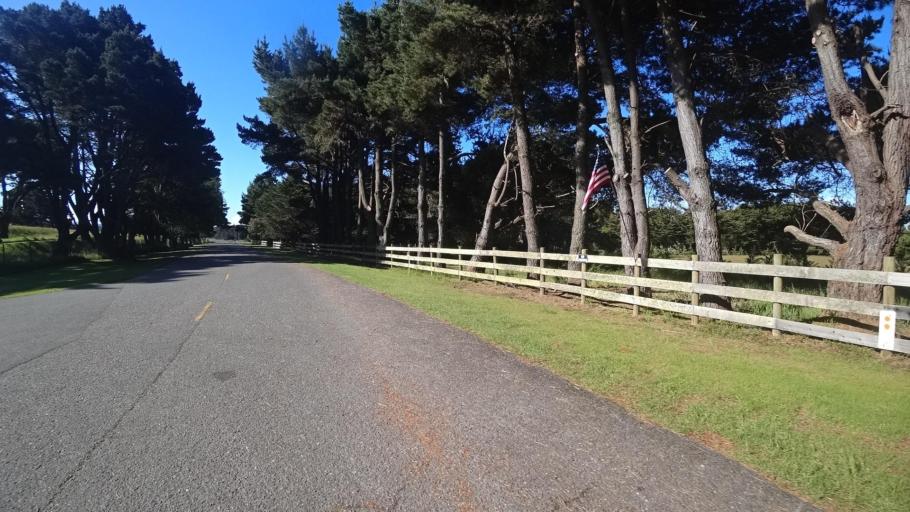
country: US
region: California
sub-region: Humboldt County
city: McKinleyville
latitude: 40.9689
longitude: -124.1167
